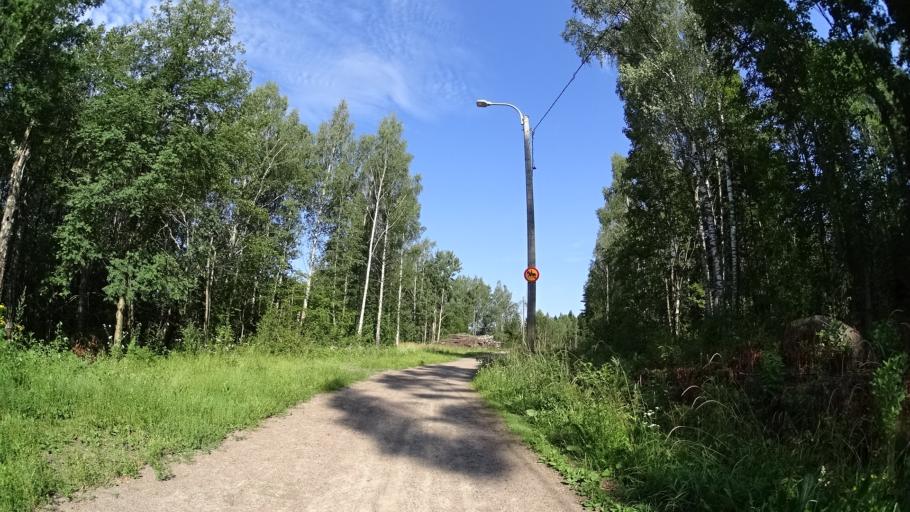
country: FI
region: Uusimaa
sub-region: Helsinki
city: Kilo
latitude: 60.2898
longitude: 24.8233
